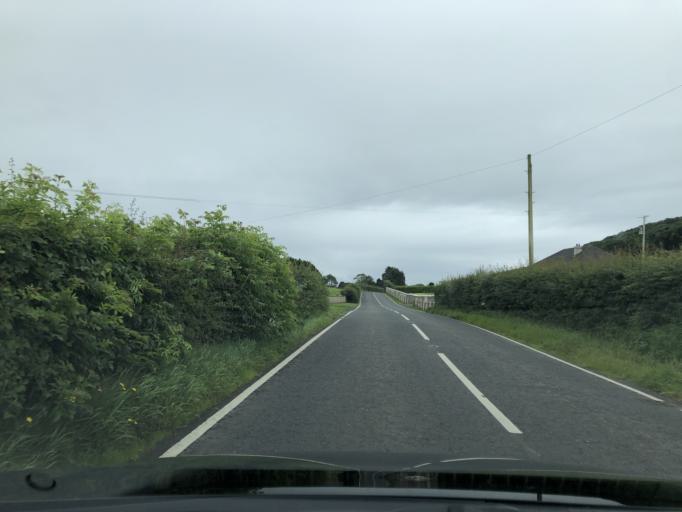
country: GB
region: Northern Ireland
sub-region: Down District
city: Dundrum
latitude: 54.2693
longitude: -5.7856
